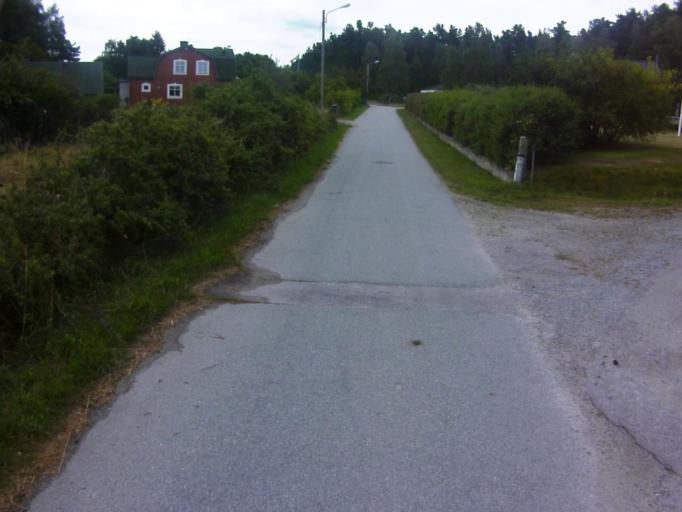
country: SE
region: Blekinge
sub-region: Karlshamns Kommun
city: Morrum
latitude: 56.0687
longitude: 14.7186
